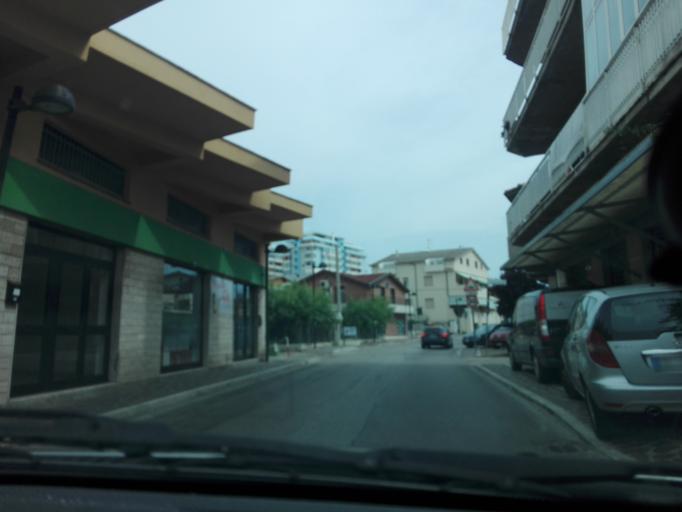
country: IT
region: Abruzzo
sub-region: Provincia di Pescara
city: Villa Raspa
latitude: 42.4943
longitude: 14.1796
